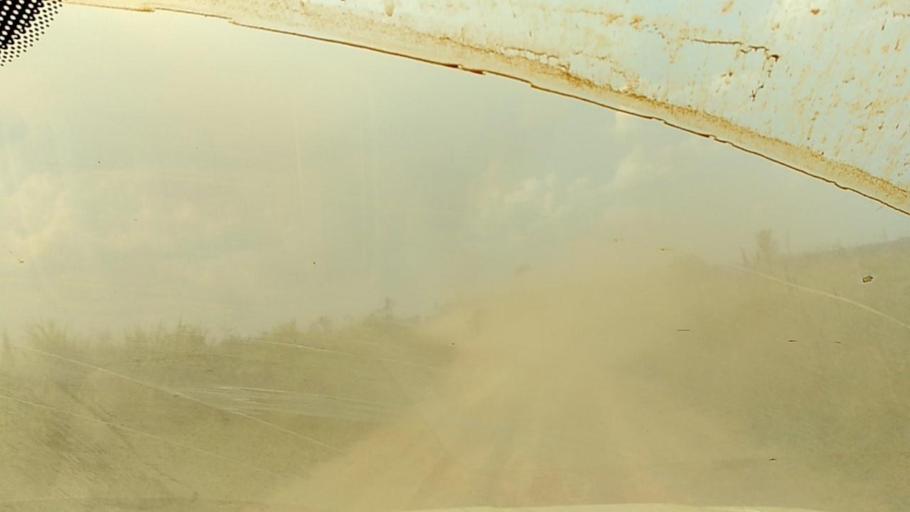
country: BR
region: Rondonia
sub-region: Porto Velho
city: Porto Velho
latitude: -8.6893
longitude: -63.2391
